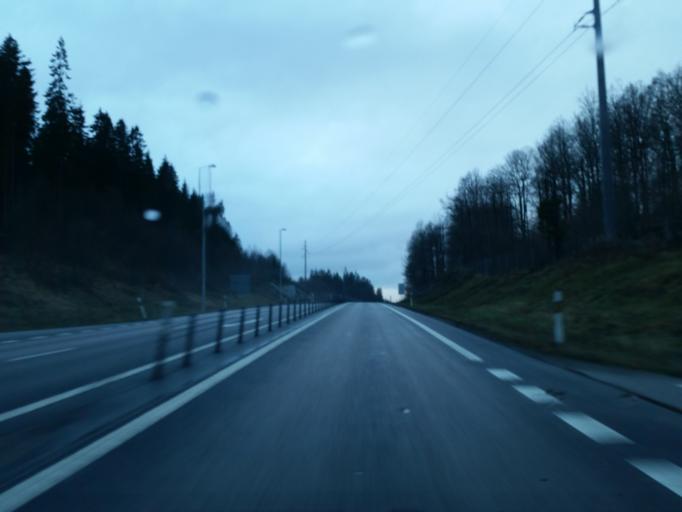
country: SE
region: Vaestra Goetaland
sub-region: Boras Kommun
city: Ganghester
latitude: 57.6756
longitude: 12.9857
